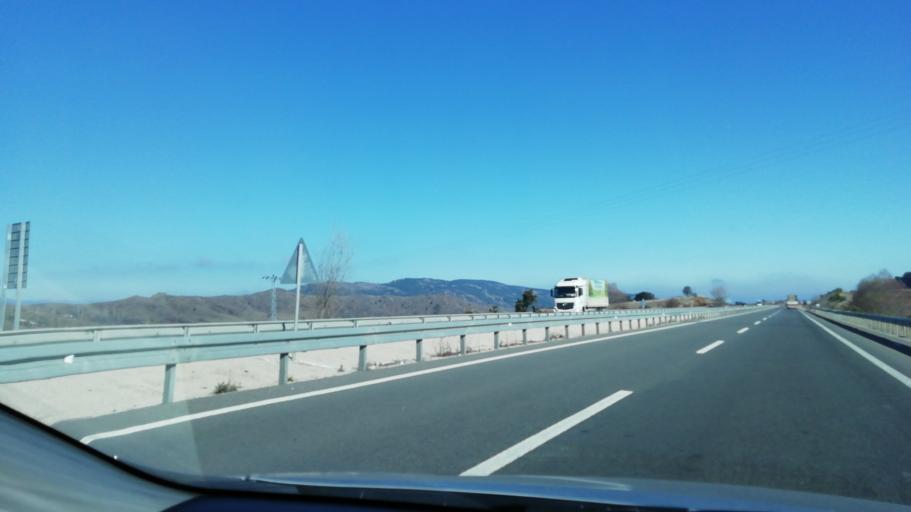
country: TR
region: Karabuk
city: Gozyeri
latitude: 40.8617
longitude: 32.5088
